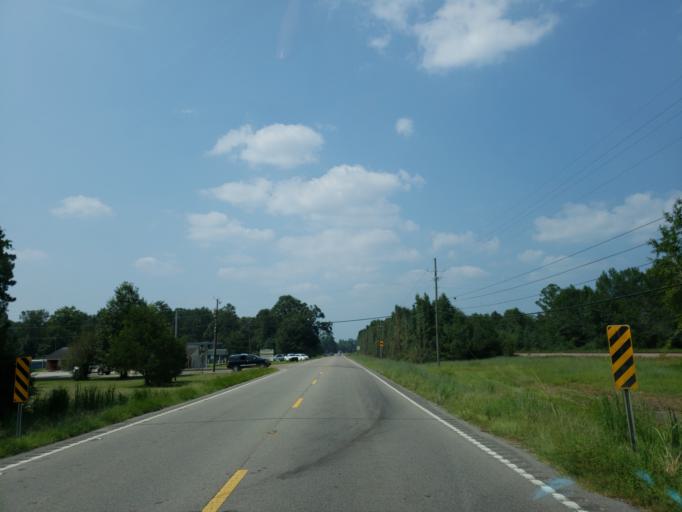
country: US
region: Mississippi
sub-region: Forrest County
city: Glendale
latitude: 31.4360
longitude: -89.2845
